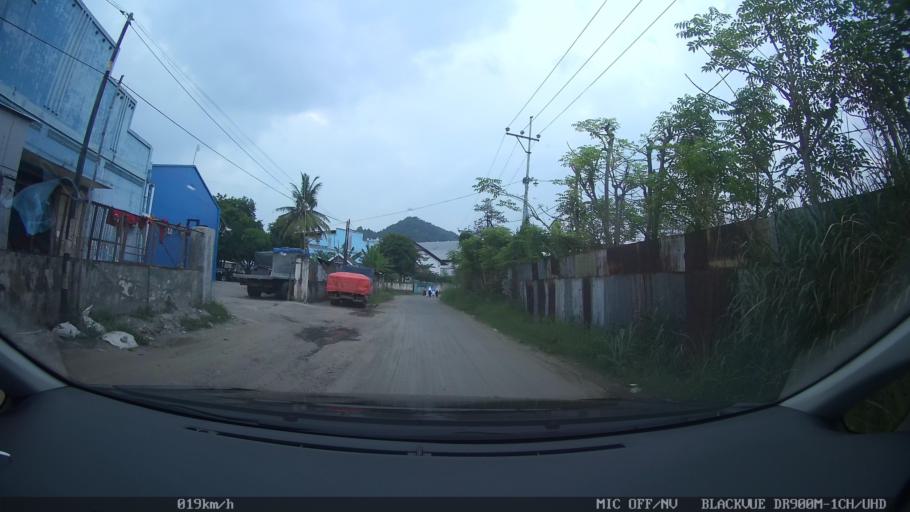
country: ID
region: Lampung
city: Bandarlampung
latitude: -5.4401
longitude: 105.2908
